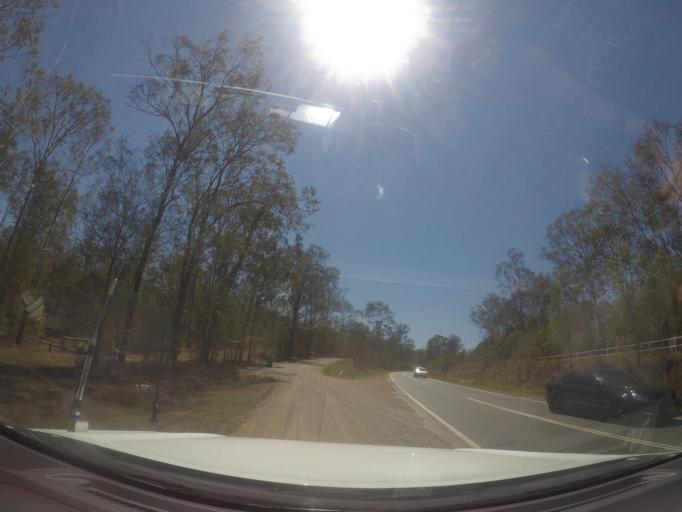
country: AU
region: Queensland
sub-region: Logan
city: North Maclean
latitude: -27.8073
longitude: 153.0459
